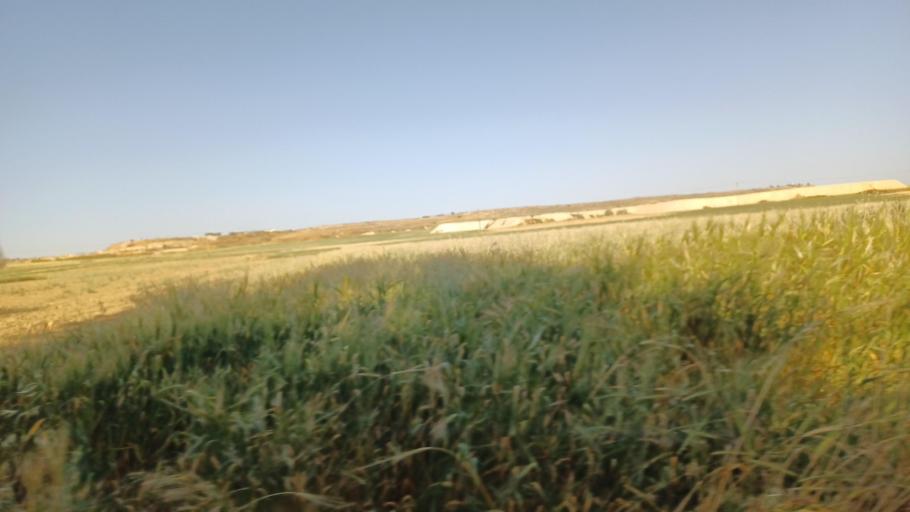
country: CY
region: Lefkosia
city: Mammari
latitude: 35.1588
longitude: 33.2476
